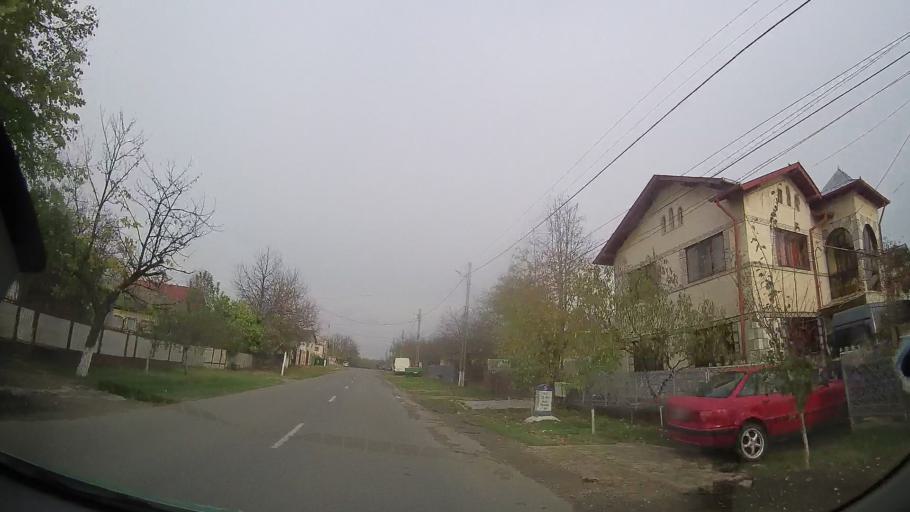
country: RO
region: Prahova
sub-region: Comuna Balta Doamnei
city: Balta Doamnei
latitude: 44.7623
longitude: 26.1428
